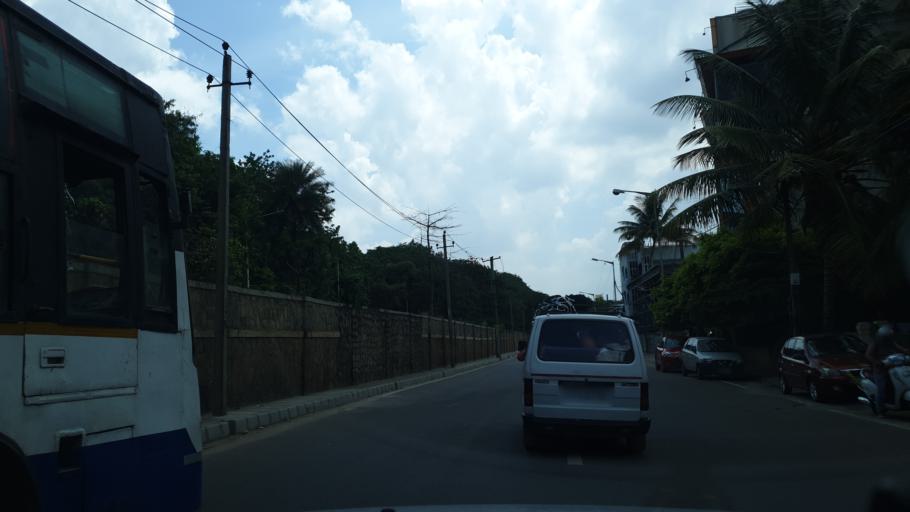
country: IN
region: Karnataka
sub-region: Bangalore Urban
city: Bangalore
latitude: 13.0237
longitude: 77.5628
